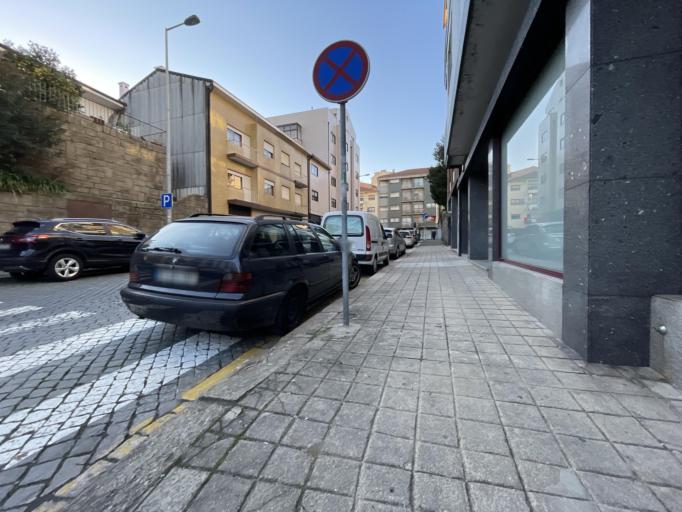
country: PT
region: Porto
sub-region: Porto
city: Porto
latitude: 41.1561
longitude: -8.5940
